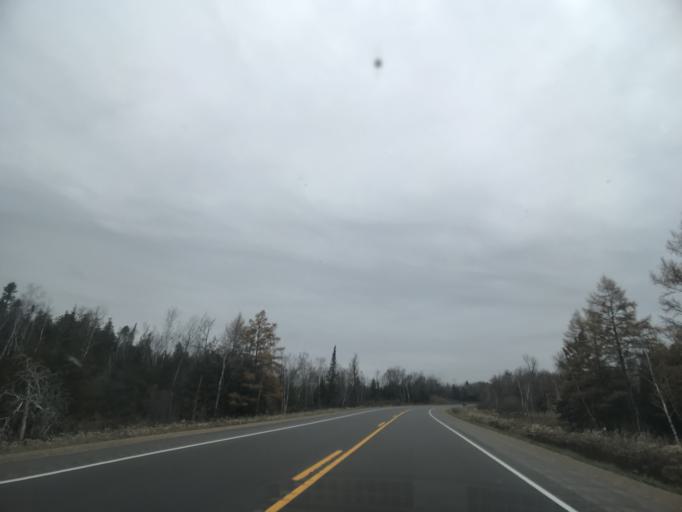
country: US
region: Wisconsin
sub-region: Menominee County
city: Legend Lake
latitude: 45.2621
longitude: -88.5134
